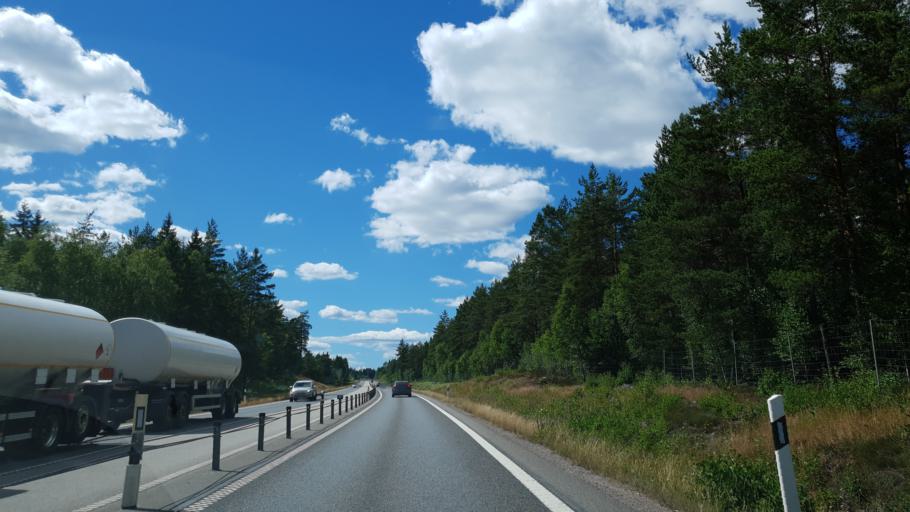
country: SE
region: Kronoberg
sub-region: Vaxjo Kommun
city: Vaexjoe
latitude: 56.8754
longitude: 14.9274
